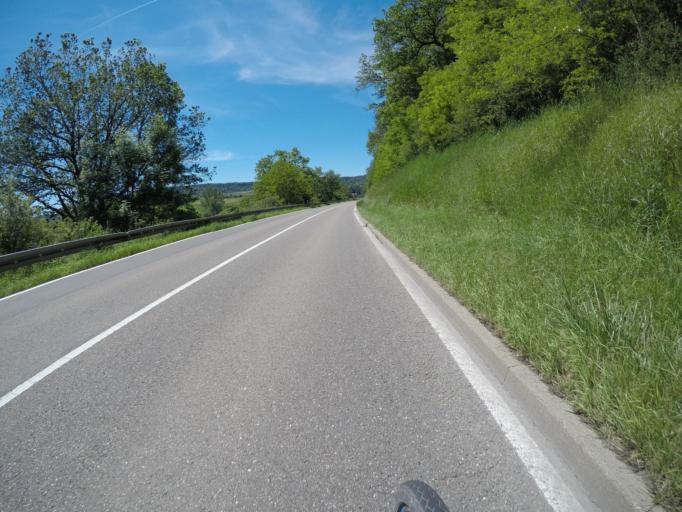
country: DE
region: Baden-Wuerttemberg
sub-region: Karlsruhe Region
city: Heimsheim
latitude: 48.7819
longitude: 8.8460
